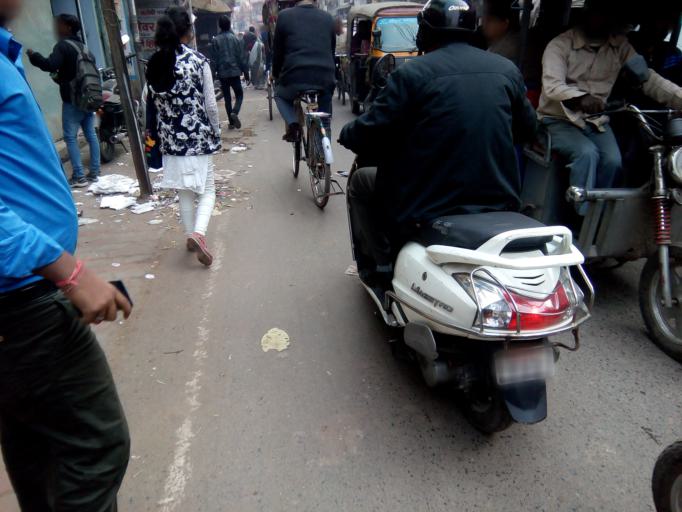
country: IN
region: Bihar
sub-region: Patna
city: Patna
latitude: 25.6158
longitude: 85.1495
